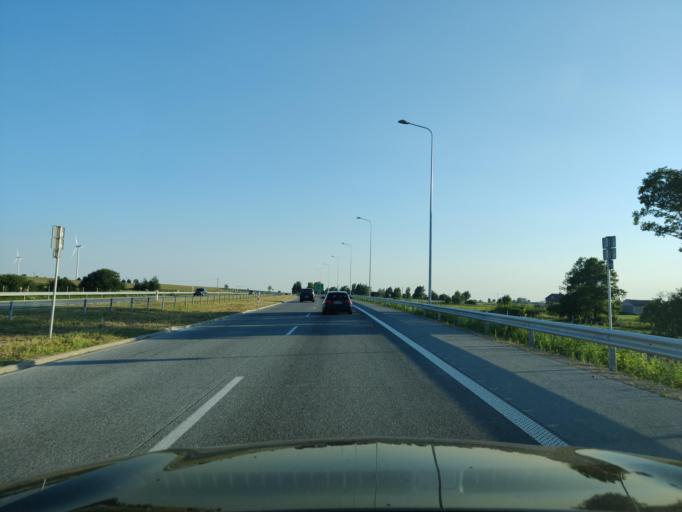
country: PL
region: Masovian Voivodeship
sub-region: Powiat mlawski
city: Wisniewo
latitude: 53.0702
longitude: 20.3718
